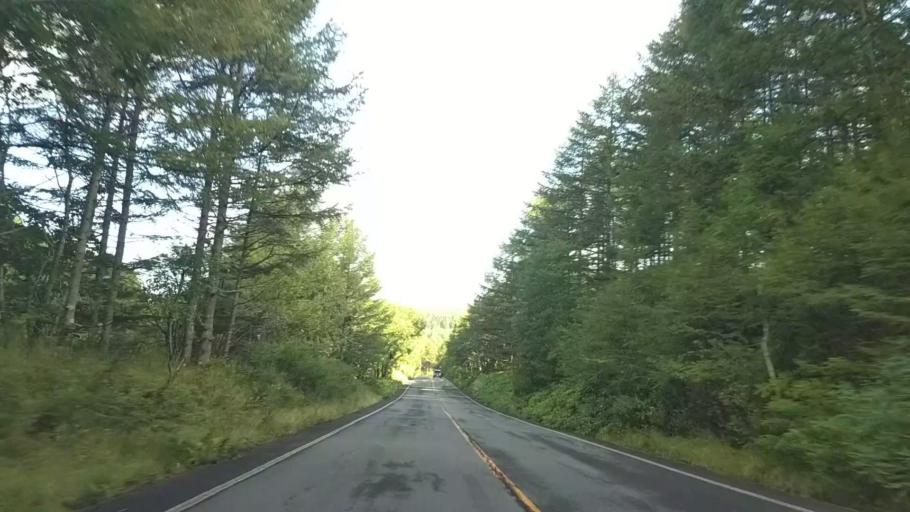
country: JP
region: Nagano
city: Suwa
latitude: 36.1063
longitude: 138.1765
